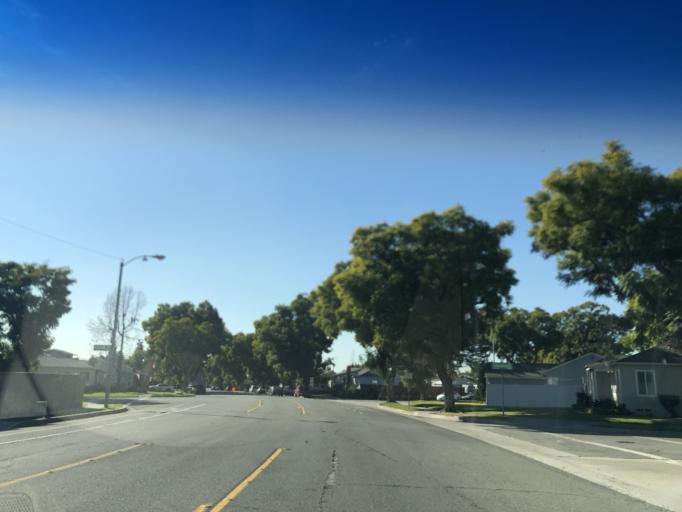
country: US
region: California
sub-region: Los Angeles County
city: South Whittier
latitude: 33.9479
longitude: -118.0161
